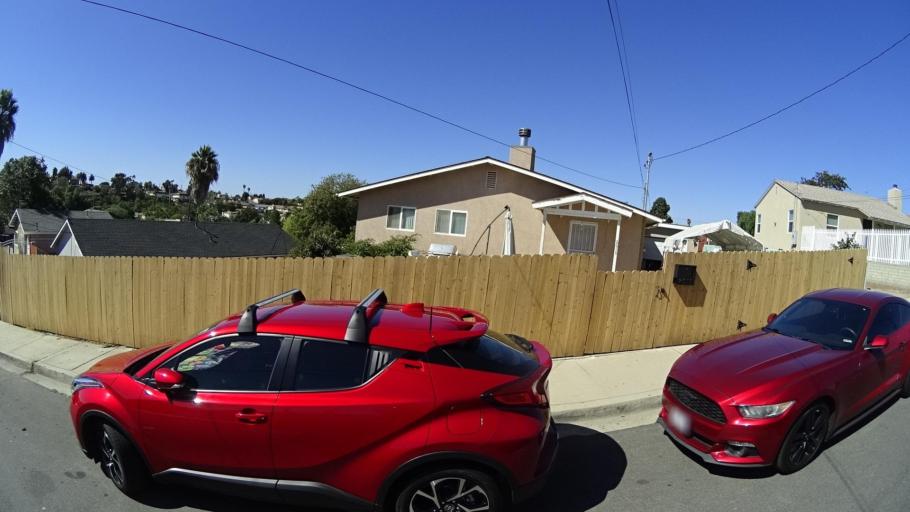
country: US
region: California
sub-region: San Diego County
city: National City
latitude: 32.6688
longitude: -117.0746
